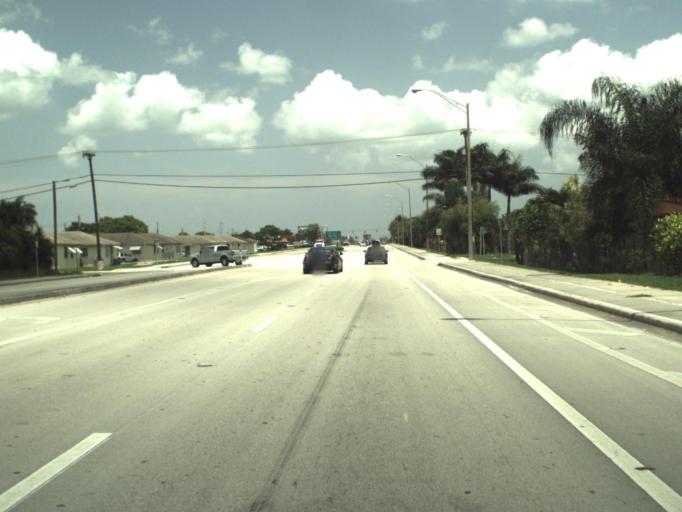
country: US
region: Florida
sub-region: Palm Beach County
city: Belle Glade
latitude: 26.6924
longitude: -80.6677
